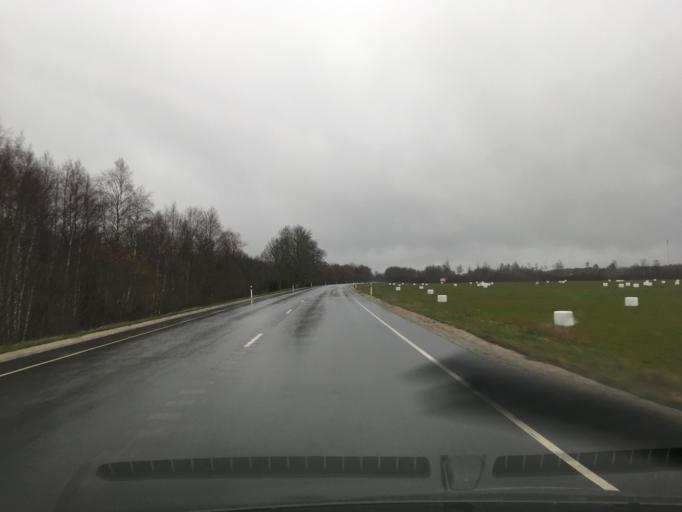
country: EE
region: Laeaene
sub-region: Lihula vald
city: Lihula
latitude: 58.8493
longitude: 24.0672
